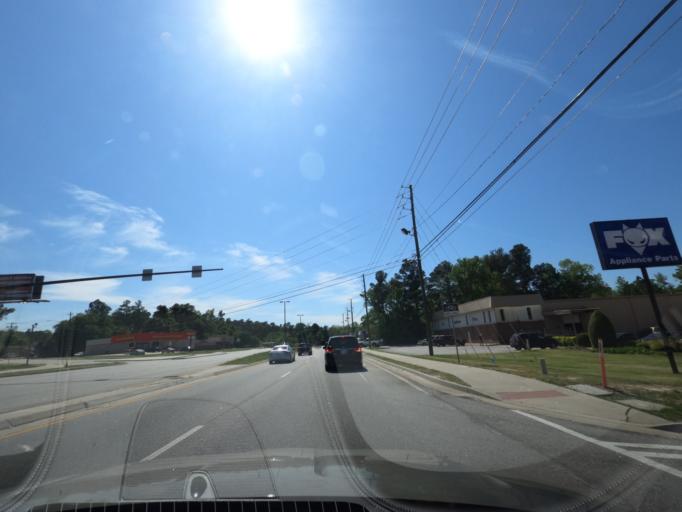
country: US
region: Georgia
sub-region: Columbia County
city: Martinez
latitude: 33.4659
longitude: -82.0864
